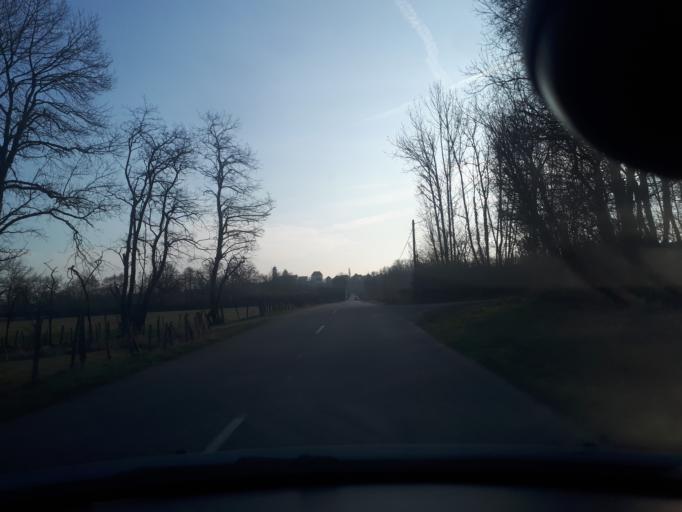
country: FR
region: Rhone-Alpes
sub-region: Departement de l'Isere
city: Creys-Mepieu
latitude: 45.7017
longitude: 5.5327
